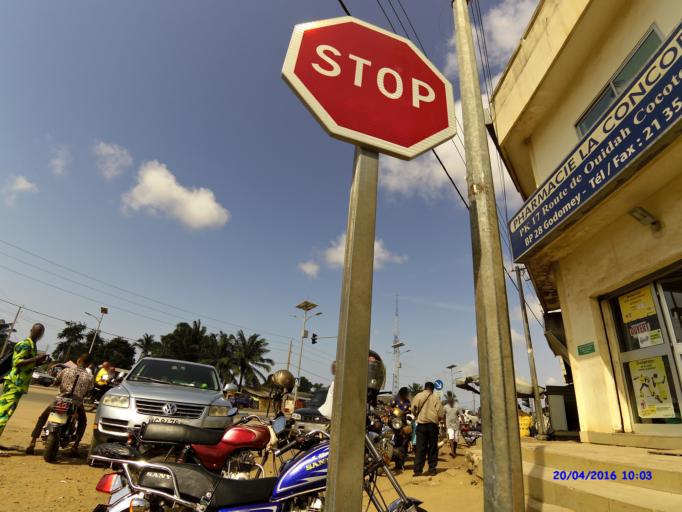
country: BJ
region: Atlantique
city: Hevie
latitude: 6.3885
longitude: 2.3008
